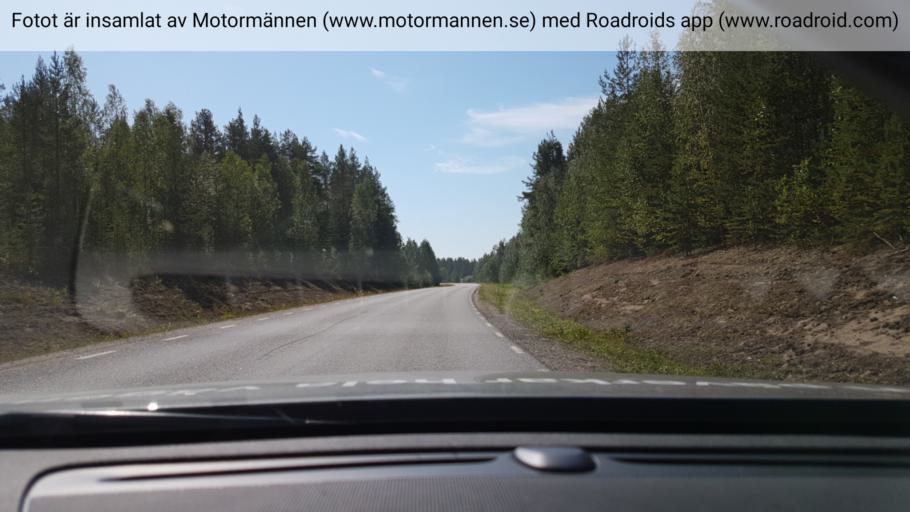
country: SE
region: Vaesterbotten
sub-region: Vindelns Kommun
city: Vindeln
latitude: 64.2897
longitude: 19.6202
